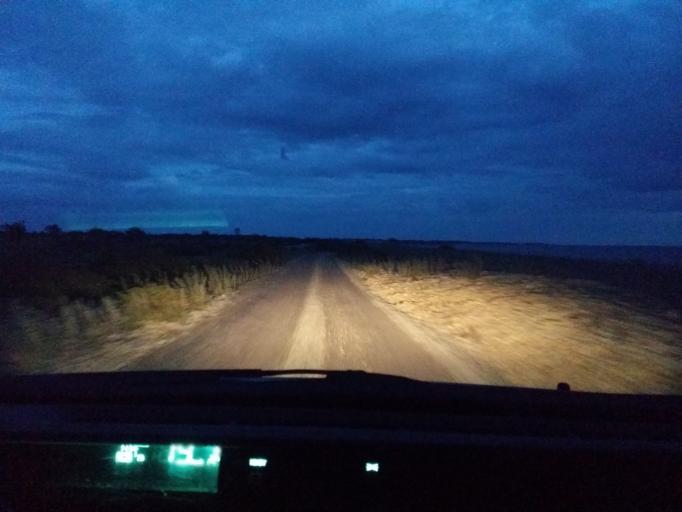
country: SE
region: Kalmar
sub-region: Borgholms Kommun
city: Borgholm
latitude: 57.1269
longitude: 16.9003
